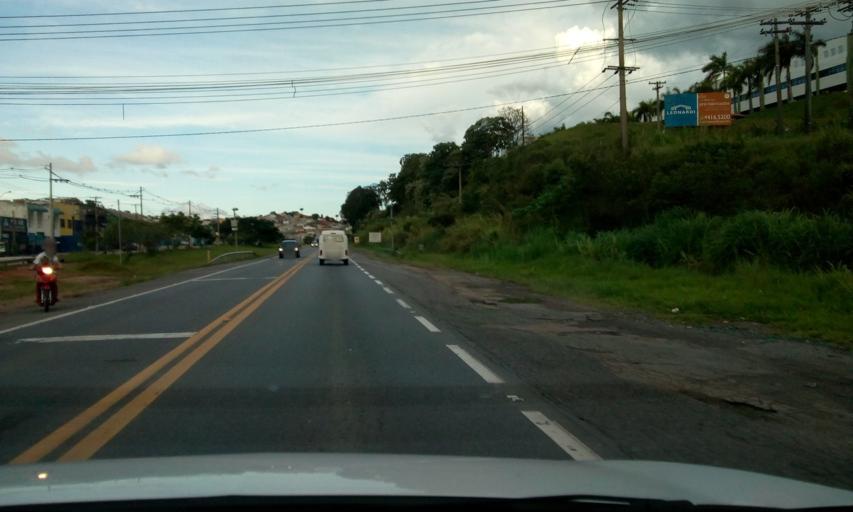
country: BR
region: Sao Paulo
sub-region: Itatiba
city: Itatiba
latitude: -23.0143
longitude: -46.8324
